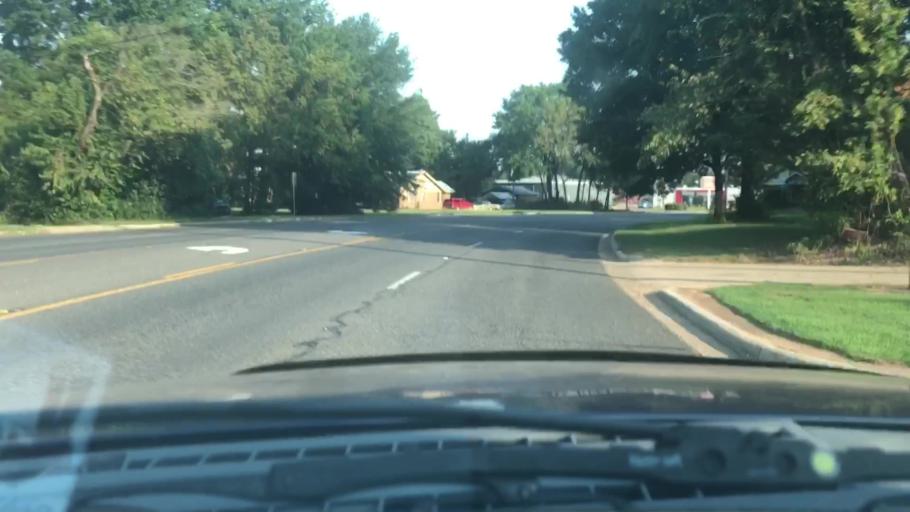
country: US
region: Texas
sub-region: Bowie County
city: Texarkana
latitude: 33.4332
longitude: -94.0624
